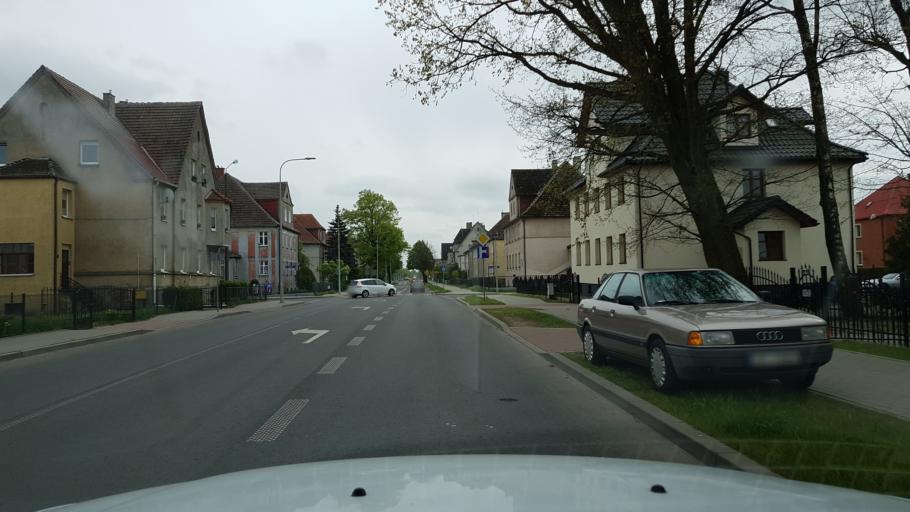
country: PL
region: West Pomeranian Voivodeship
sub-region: Powiat slawienski
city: Slawno
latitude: 54.3676
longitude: 16.6740
